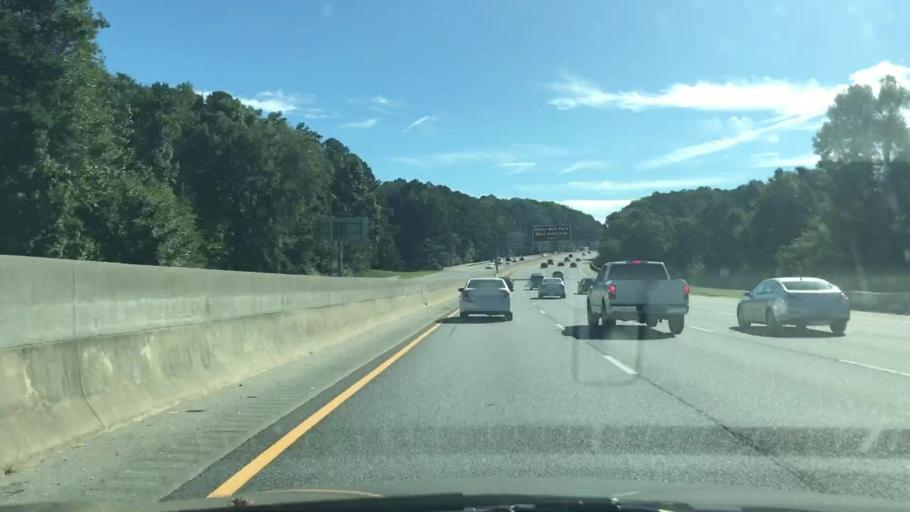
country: US
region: Georgia
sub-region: DeKalb County
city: Stone Mountain
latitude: 33.8237
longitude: -84.1548
